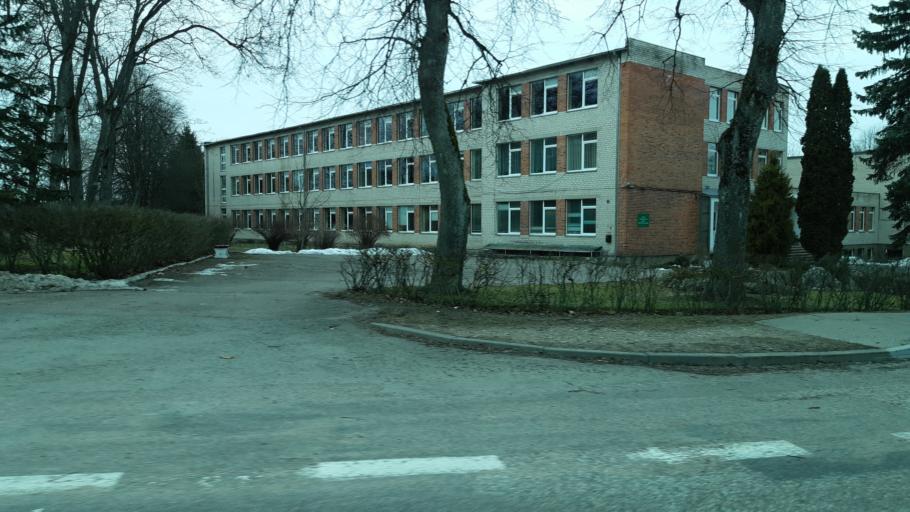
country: LT
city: Kybartai
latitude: 54.4572
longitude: 22.7109
